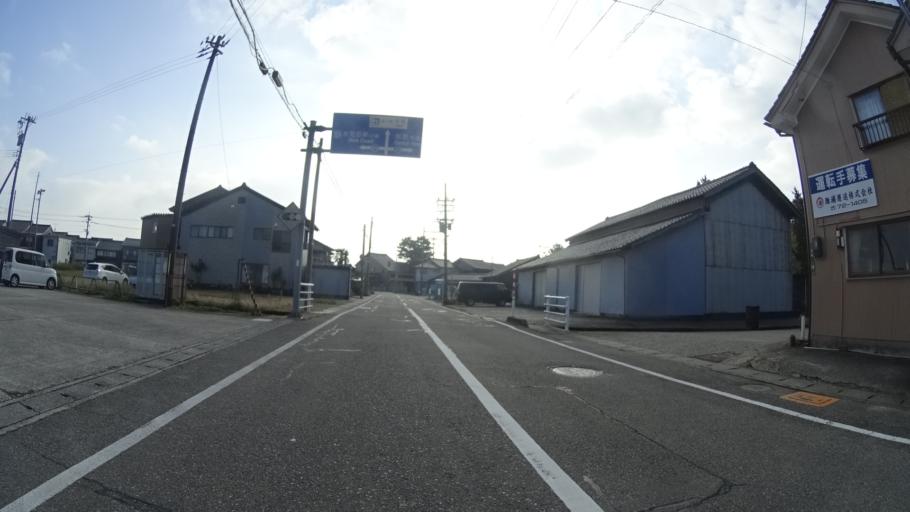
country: JP
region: Toyama
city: Himi
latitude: 36.8723
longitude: 136.9820
